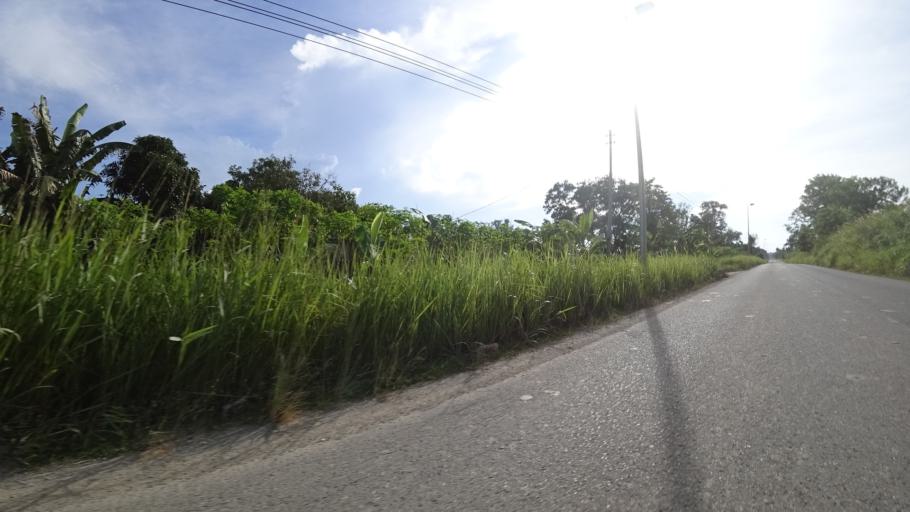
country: BN
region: Brunei and Muara
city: Bandar Seri Begawan
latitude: 4.8449
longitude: 114.8582
